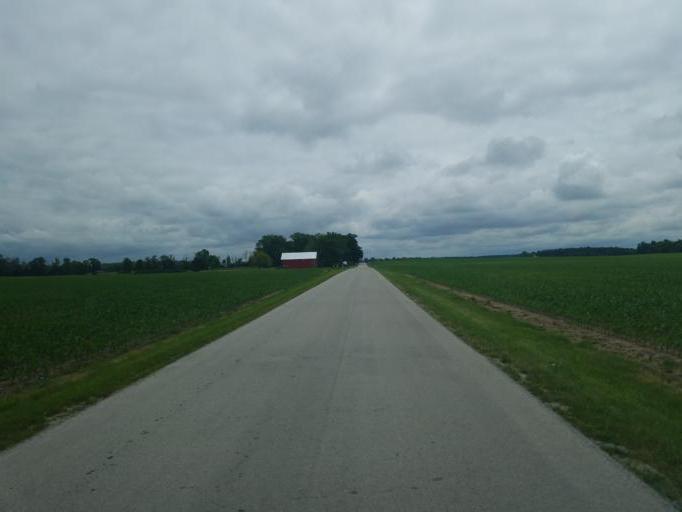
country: US
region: Ohio
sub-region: Crawford County
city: Bucyrus
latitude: 40.7752
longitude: -83.1084
